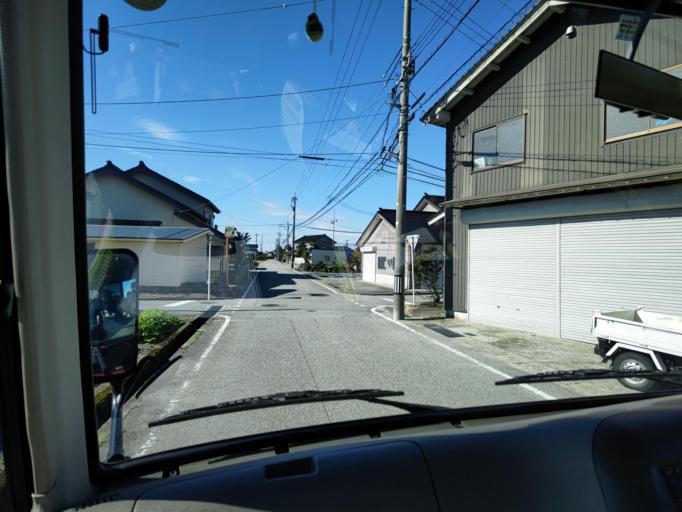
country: JP
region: Toyama
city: Nyuzen
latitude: 36.9107
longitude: 137.4328
